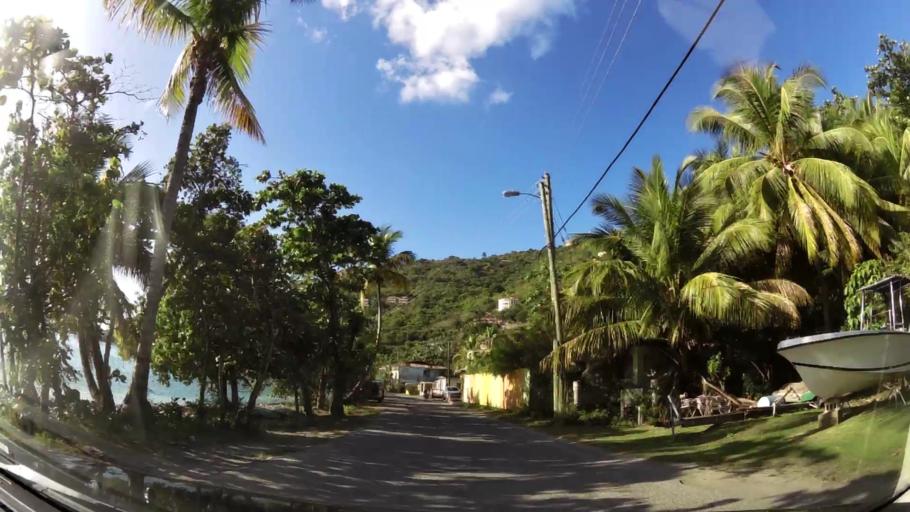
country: VG
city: Road Town
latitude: 18.4291
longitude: -64.6576
